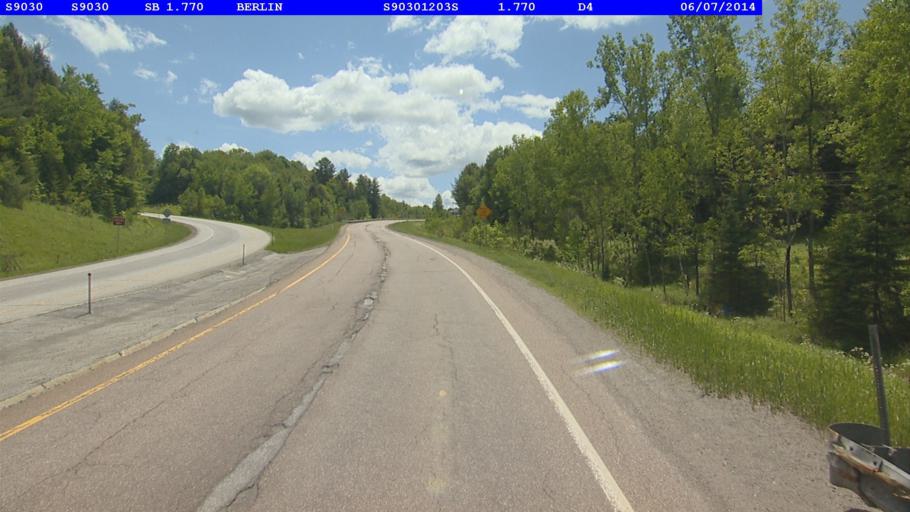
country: US
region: Vermont
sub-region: Washington County
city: Montpelier
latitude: 44.2255
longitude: -72.5580
